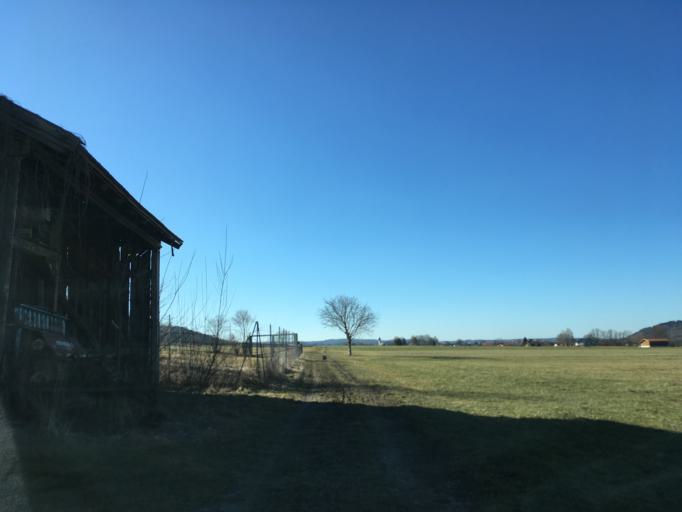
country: DE
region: Bavaria
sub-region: Upper Bavaria
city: Bruckmuhl
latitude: 47.8656
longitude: 11.9105
